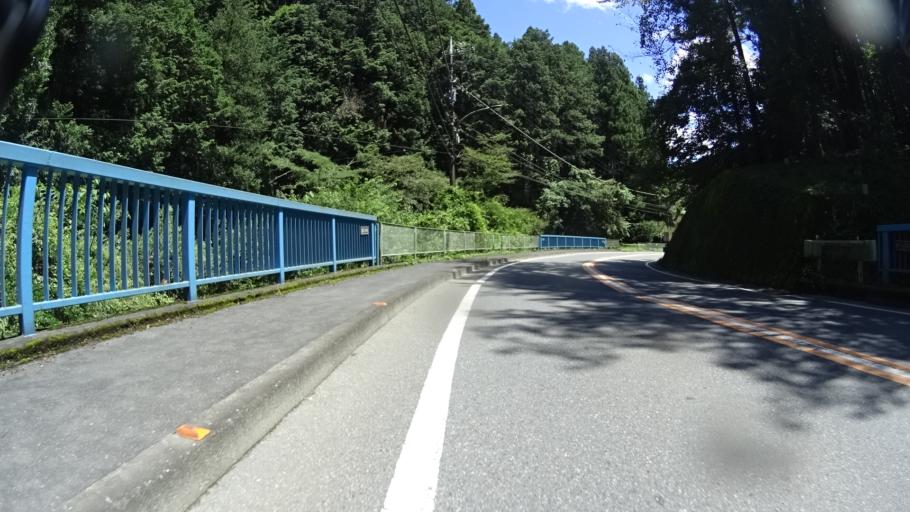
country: JP
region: Tokyo
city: Ome
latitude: 35.8268
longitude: 139.2193
